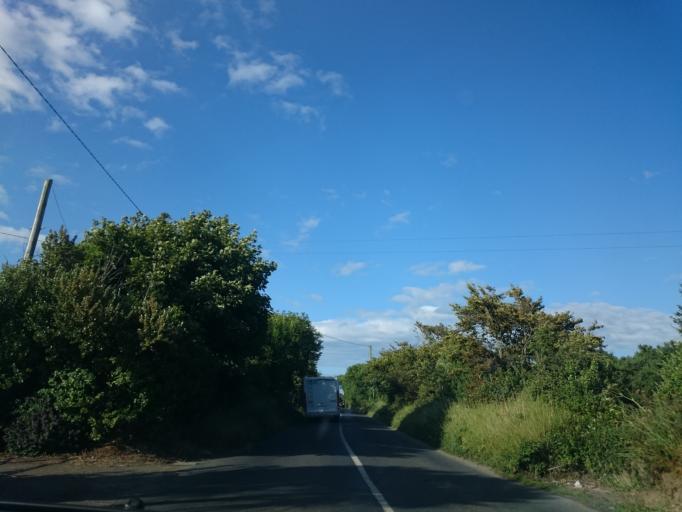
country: IE
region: Leinster
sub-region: Loch Garman
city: Loch Garman
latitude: 52.1984
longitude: -6.5567
